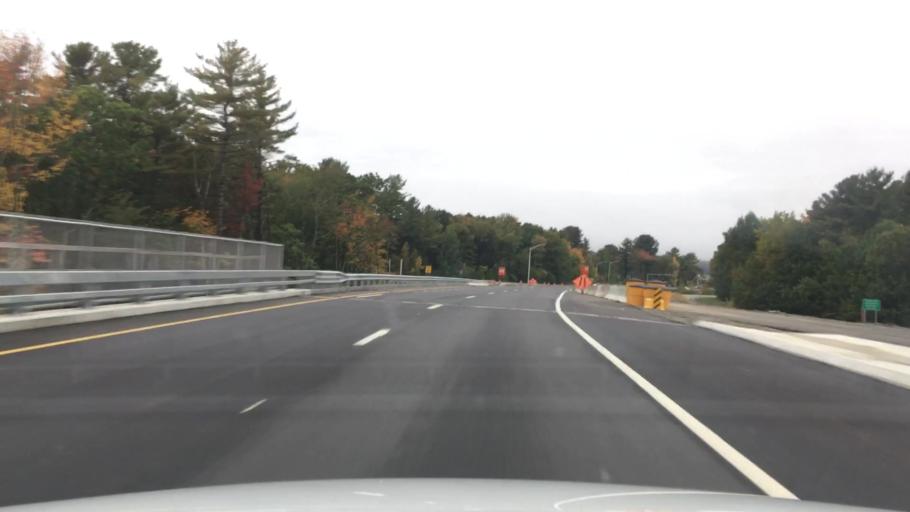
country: US
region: Maine
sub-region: York County
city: Eliot
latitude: 43.1305
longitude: -70.8389
